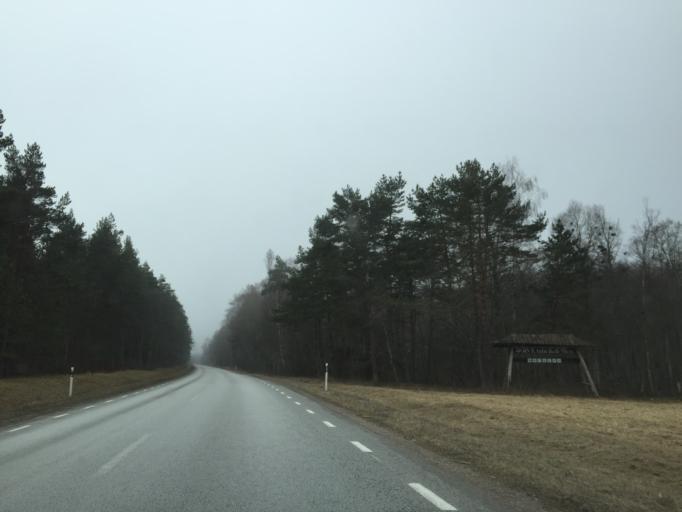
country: EE
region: Saare
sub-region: Kuressaare linn
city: Kuressaare
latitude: 58.1916
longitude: 22.2685
